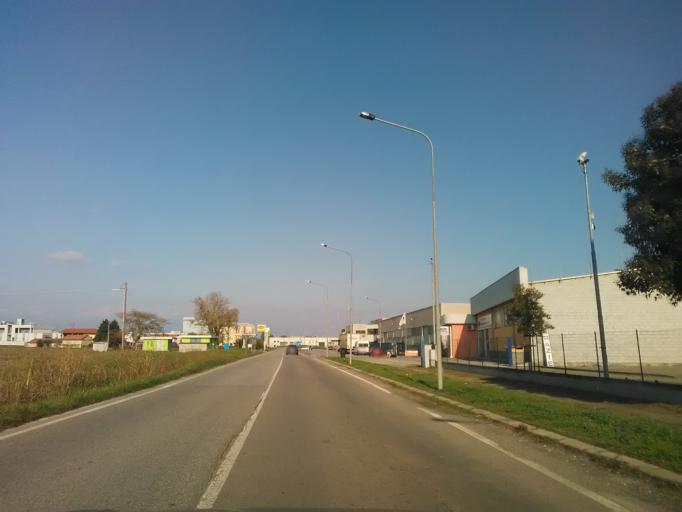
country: IT
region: Piedmont
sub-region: Provincia di Vercelli
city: Santhia
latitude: 45.3728
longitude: 8.1507
